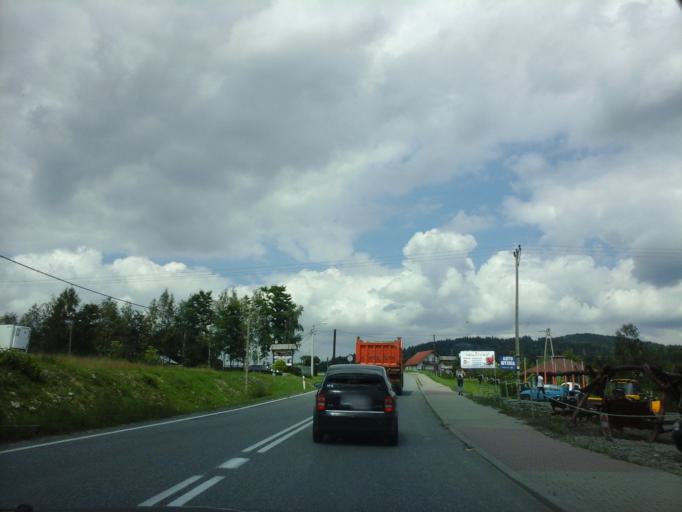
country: PL
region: Lesser Poland Voivodeship
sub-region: Powiat suski
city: Jordanow
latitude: 49.6522
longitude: 19.8202
